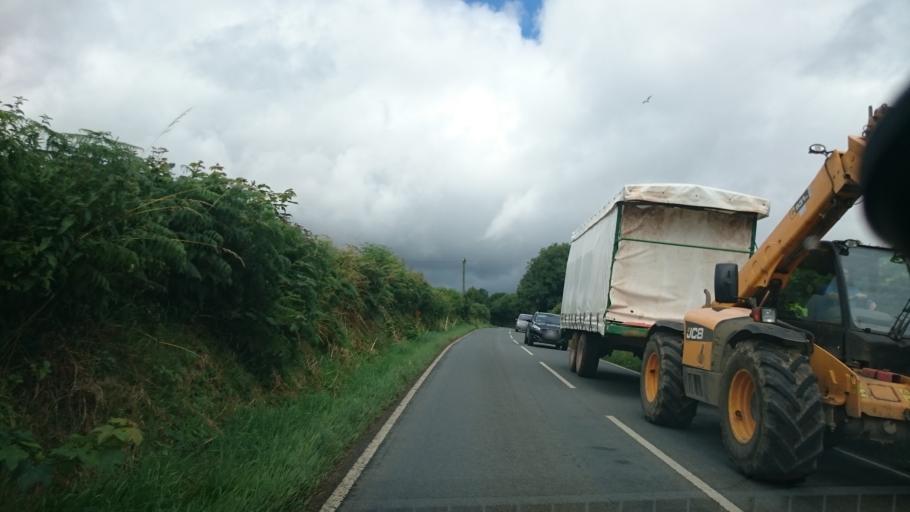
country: GB
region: Wales
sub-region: Pembrokeshire
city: Burton
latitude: 51.7319
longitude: -4.9212
